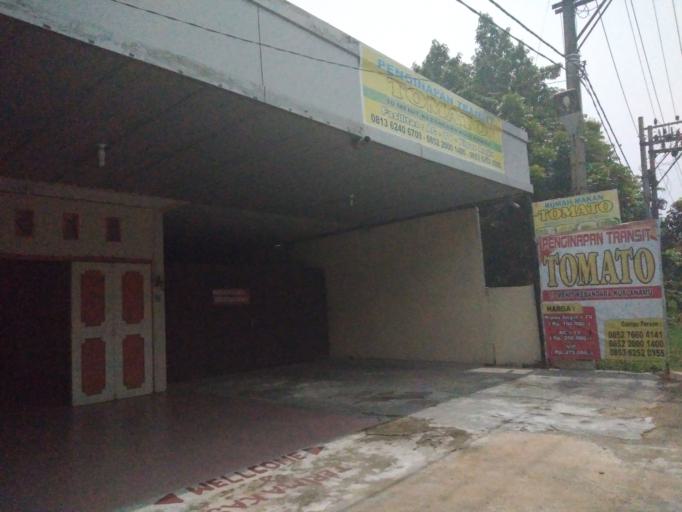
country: ID
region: North Sumatra
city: Percut
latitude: 3.5793
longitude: 98.8017
